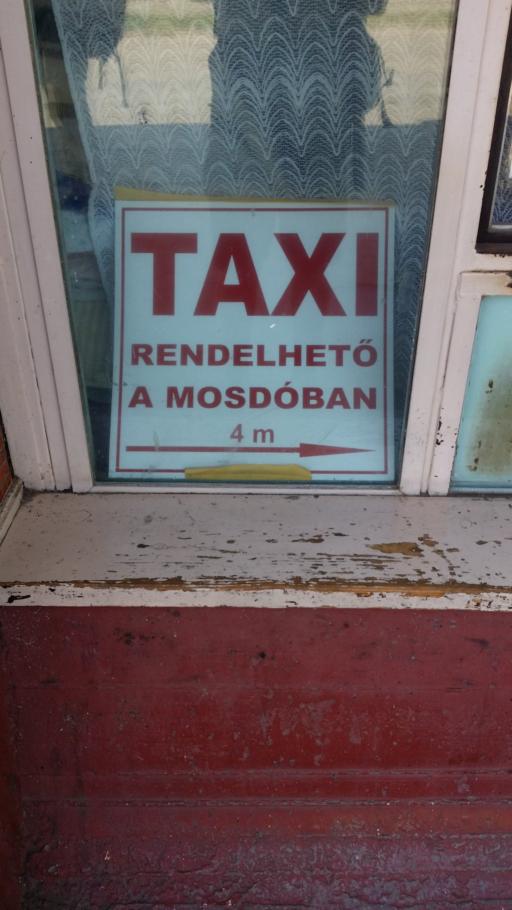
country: HU
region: Tolna
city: Dunafoldvar
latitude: 46.8058
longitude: 18.9262
